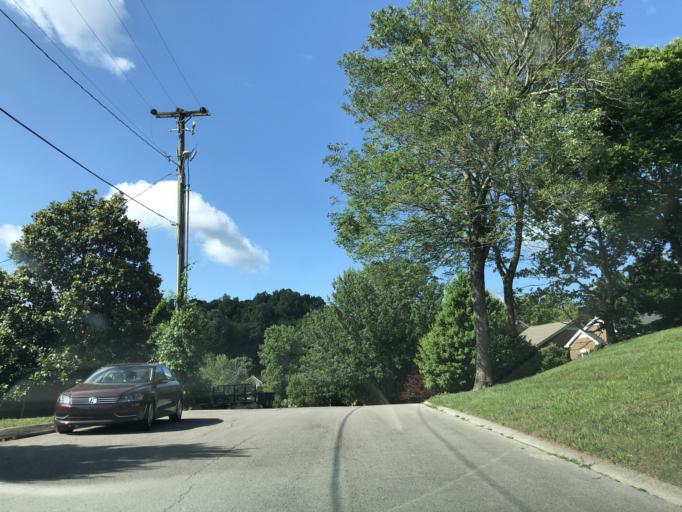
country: US
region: Tennessee
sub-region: Cheatham County
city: Pegram
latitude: 36.0627
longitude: -86.9568
